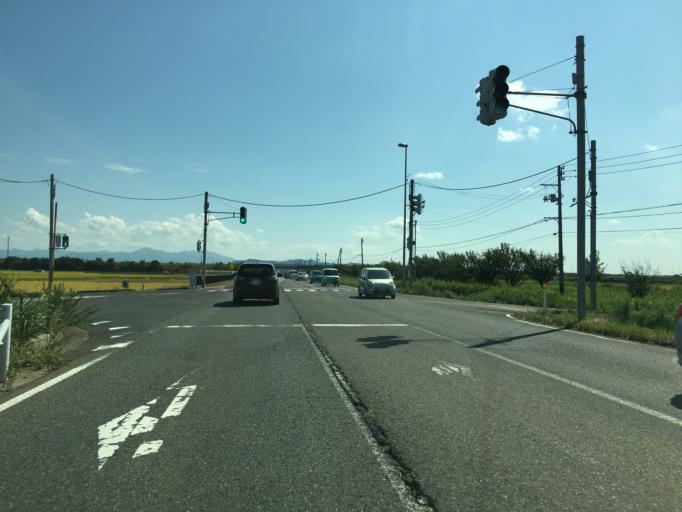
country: JP
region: Niigata
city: Niitsu-honcho
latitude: 37.8255
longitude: 139.0982
